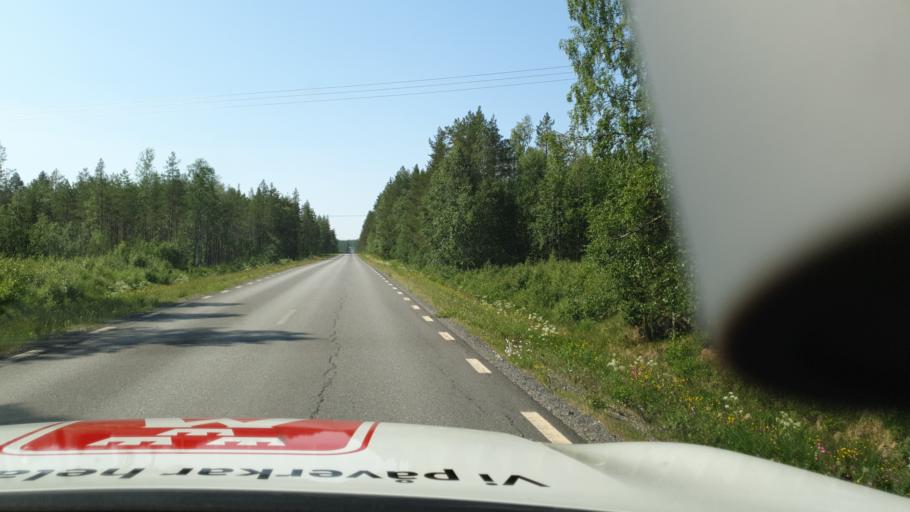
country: SE
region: Vaesterbotten
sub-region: Skelleftea Kommun
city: Langsele
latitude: 64.9867
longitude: 20.0785
